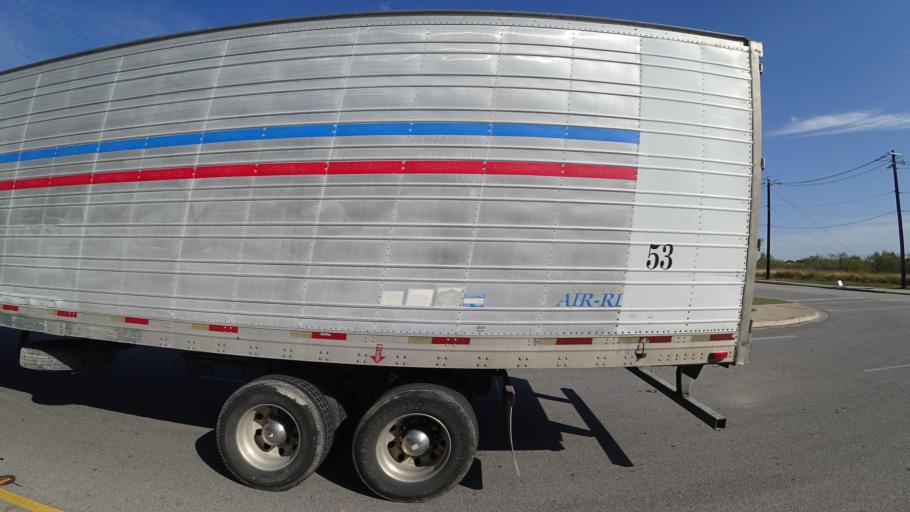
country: US
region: Texas
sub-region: Travis County
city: Pflugerville
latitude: 30.3992
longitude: -97.6334
